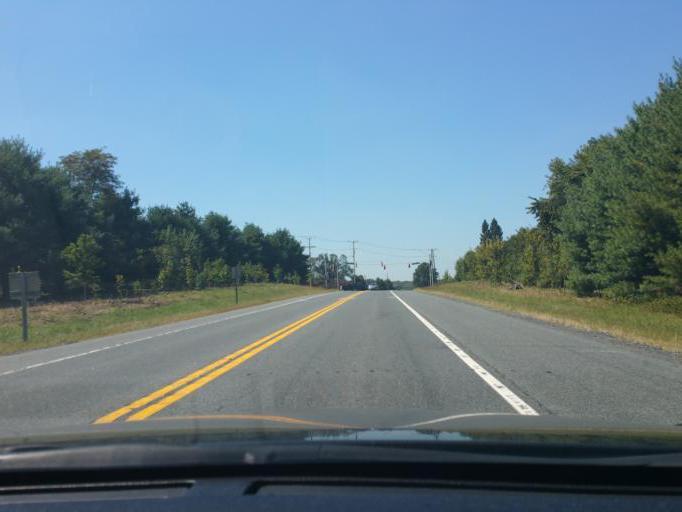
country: US
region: Maryland
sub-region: Harford County
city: Aberdeen
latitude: 39.5728
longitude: -76.1673
